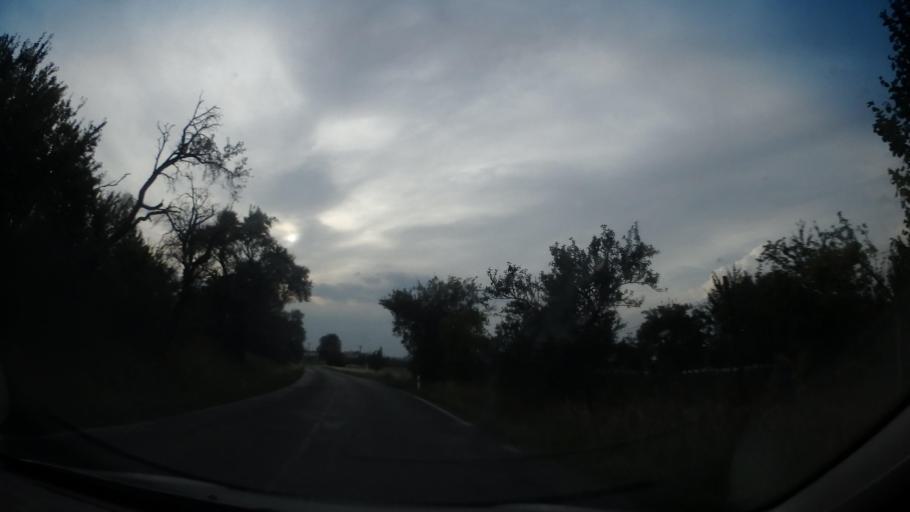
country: CZ
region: Central Bohemia
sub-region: Okres Kutna Hora
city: Caslav
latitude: 49.9027
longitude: 15.4135
